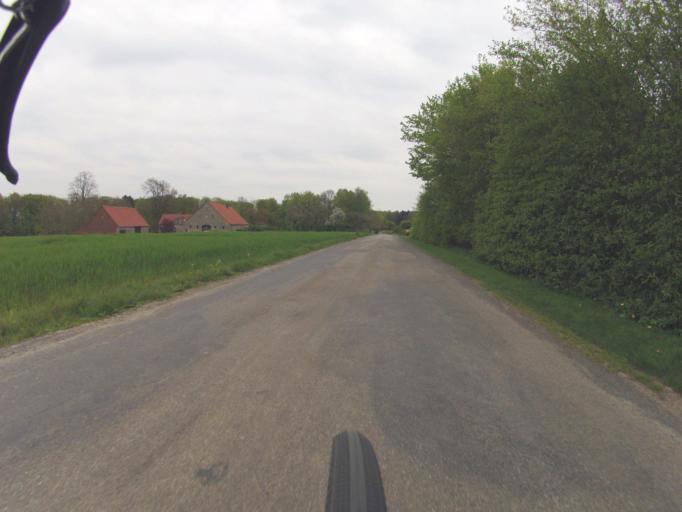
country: DE
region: North Rhine-Westphalia
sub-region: Regierungsbezirk Munster
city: Mettingen
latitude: 52.2953
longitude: 7.7896
